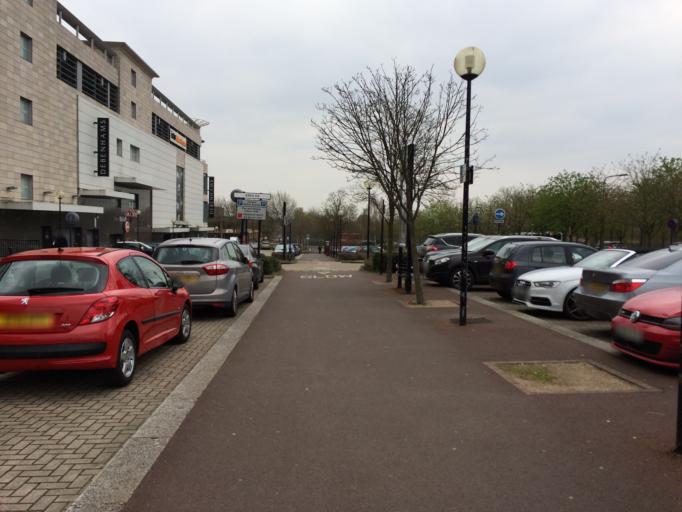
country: GB
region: England
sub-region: Milton Keynes
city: Milton Keynes
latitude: 52.0403
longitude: -0.7582
